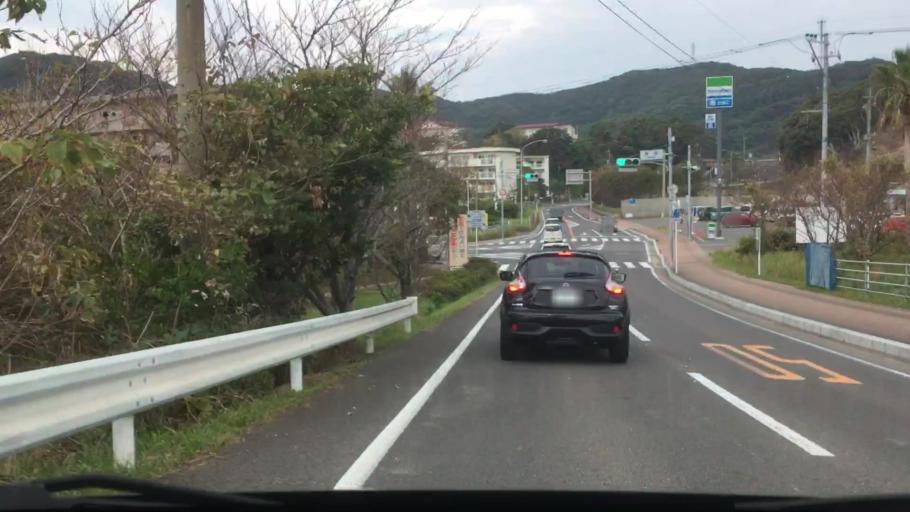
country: JP
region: Nagasaki
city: Sasebo
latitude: 33.0376
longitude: 129.6261
